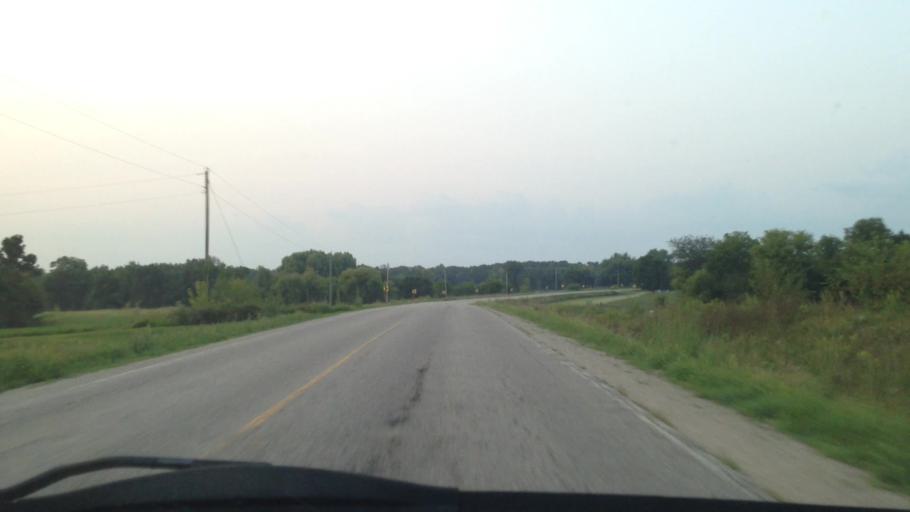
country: US
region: Iowa
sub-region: Benton County
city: Urbana
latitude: 42.1479
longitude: -91.8793
